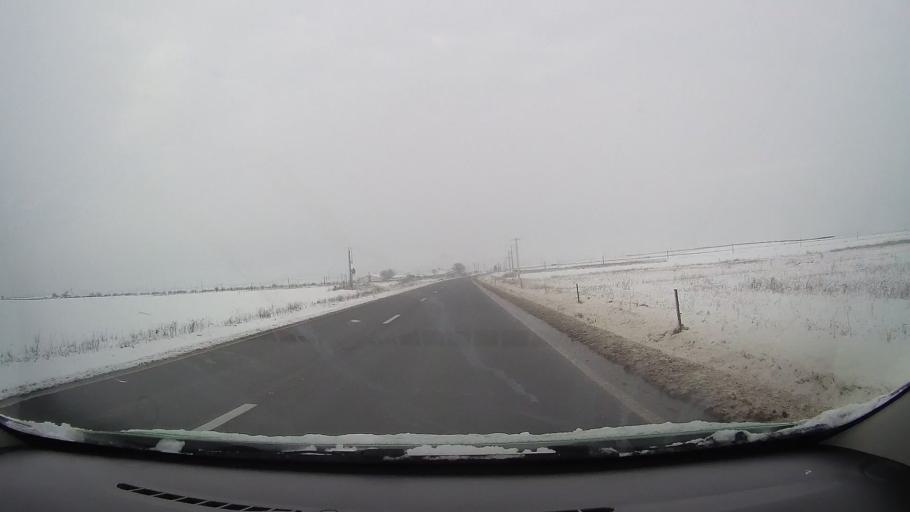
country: RO
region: Alba
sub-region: Municipiul Sebes
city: Lancram
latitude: 45.9669
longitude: 23.5300
